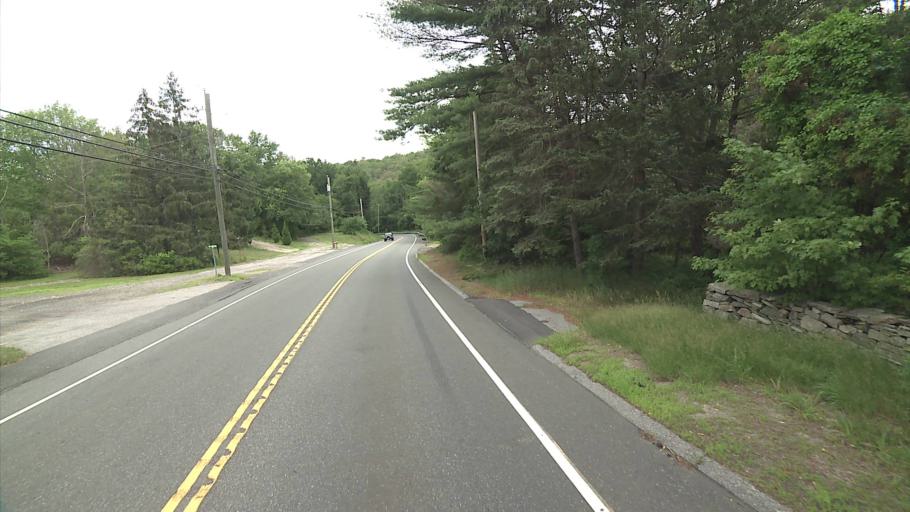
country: US
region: Connecticut
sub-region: New London County
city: Ledyard Center
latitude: 41.4697
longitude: -72.0249
